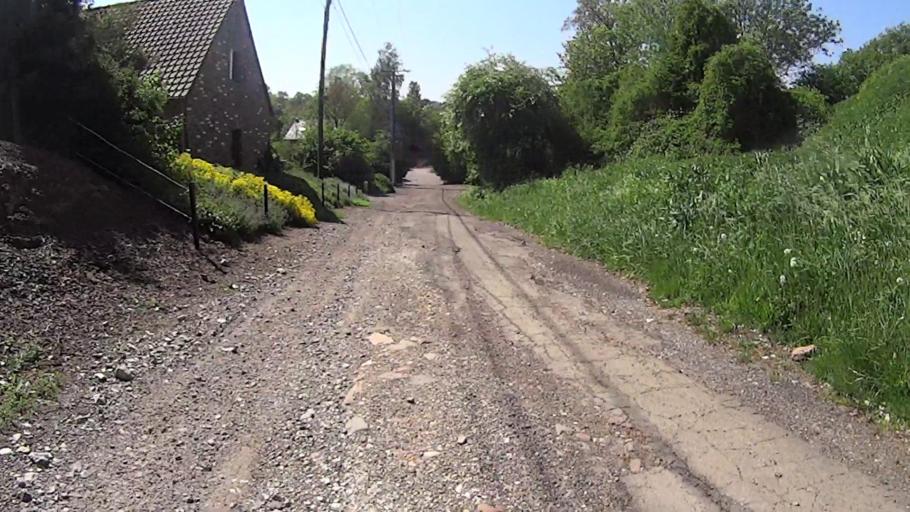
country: BE
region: Wallonia
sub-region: Province de Liege
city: Dalhem
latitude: 50.7160
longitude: 5.7554
